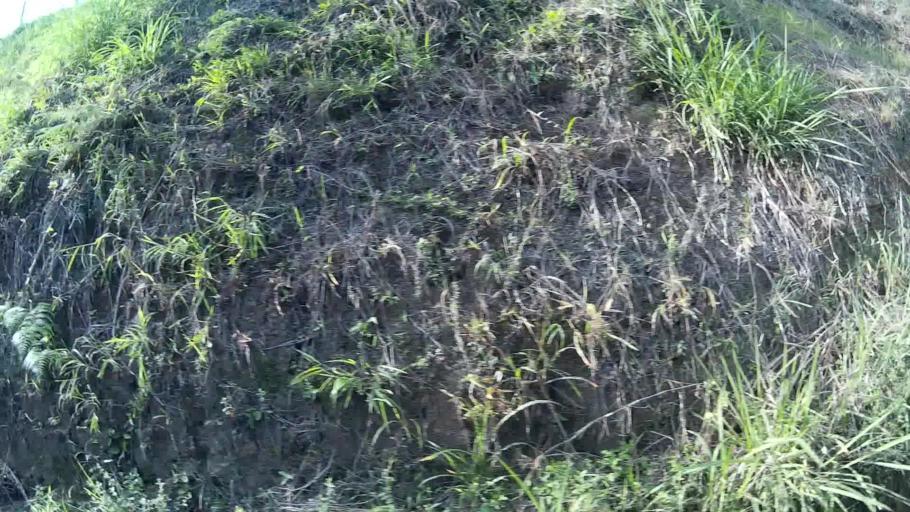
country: CO
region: Valle del Cauca
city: Ulloa
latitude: 4.7325
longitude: -75.7315
